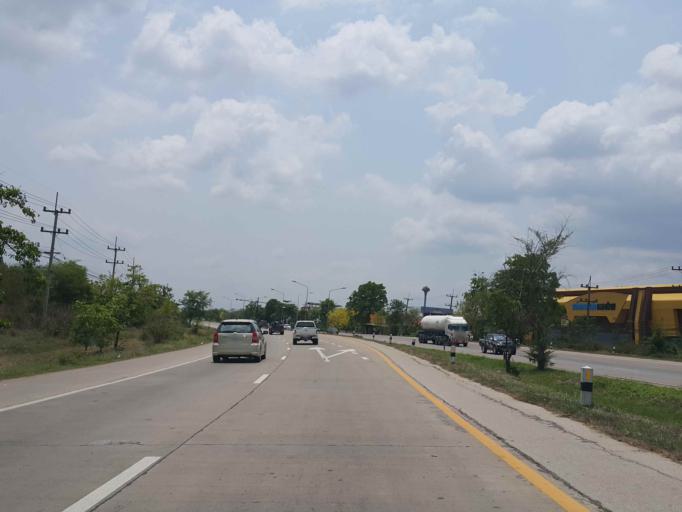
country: TH
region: Lampang
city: Ko Kha
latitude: 18.2322
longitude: 99.4312
